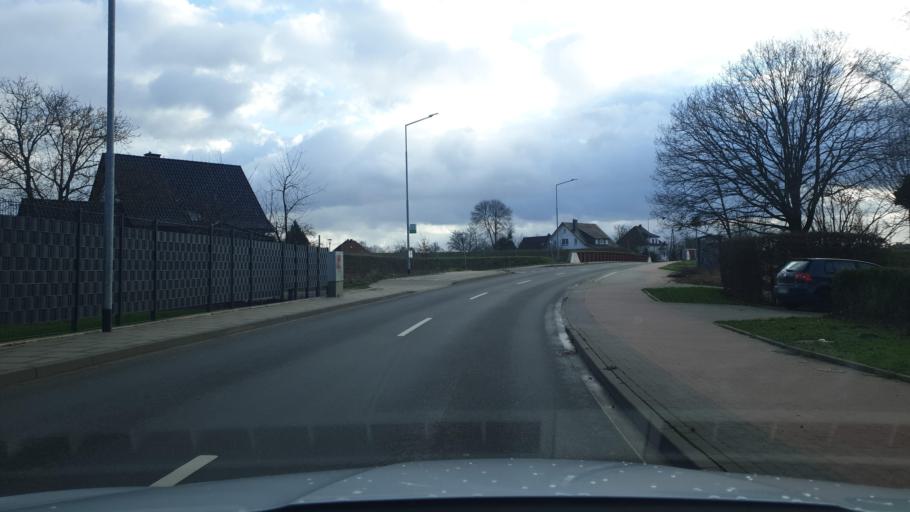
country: DE
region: North Rhine-Westphalia
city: Bad Oeynhausen
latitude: 52.2265
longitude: 8.7685
